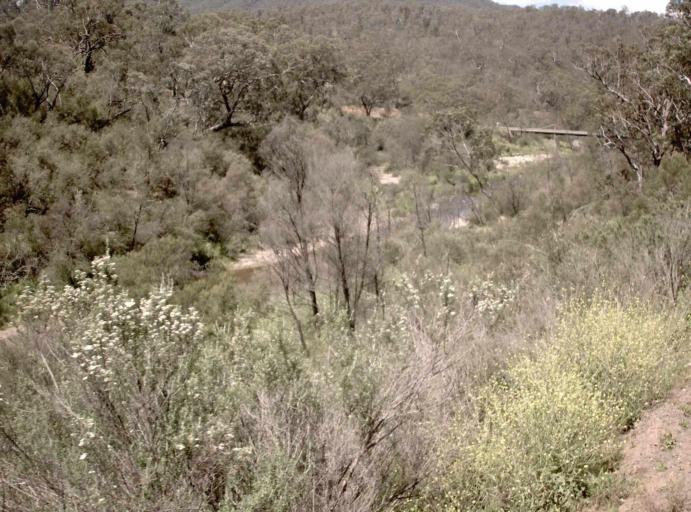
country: AU
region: New South Wales
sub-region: Snowy River
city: Jindabyne
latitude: -37.0364
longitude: 148.5457
